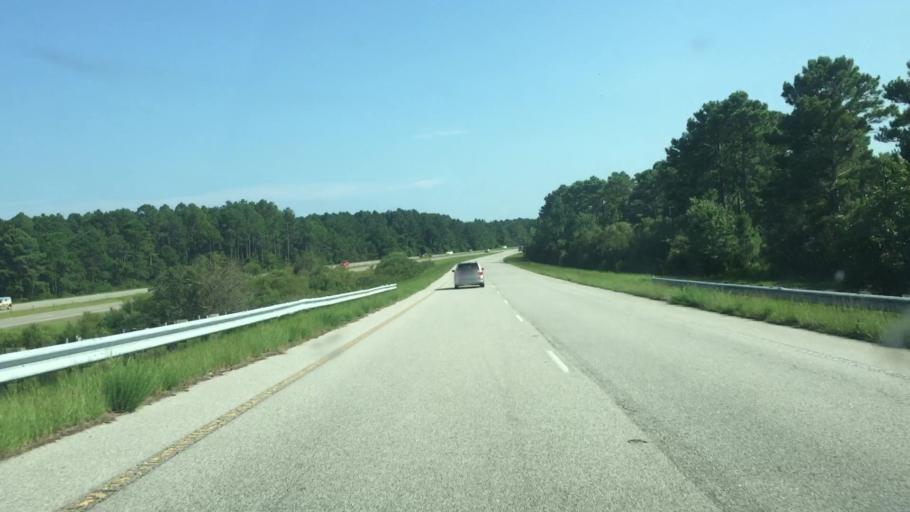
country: US
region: South Carolina
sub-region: Horry County
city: North Myrtle Beach
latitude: 33.8072
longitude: -78.7798
